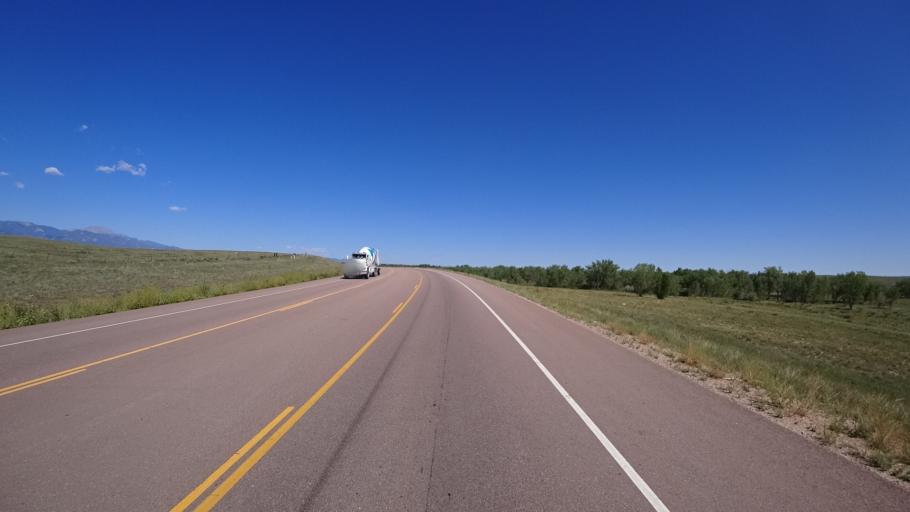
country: US
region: Colorado
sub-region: El Paso County
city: Security-Widefield
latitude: 38.7467
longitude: -104.6484
